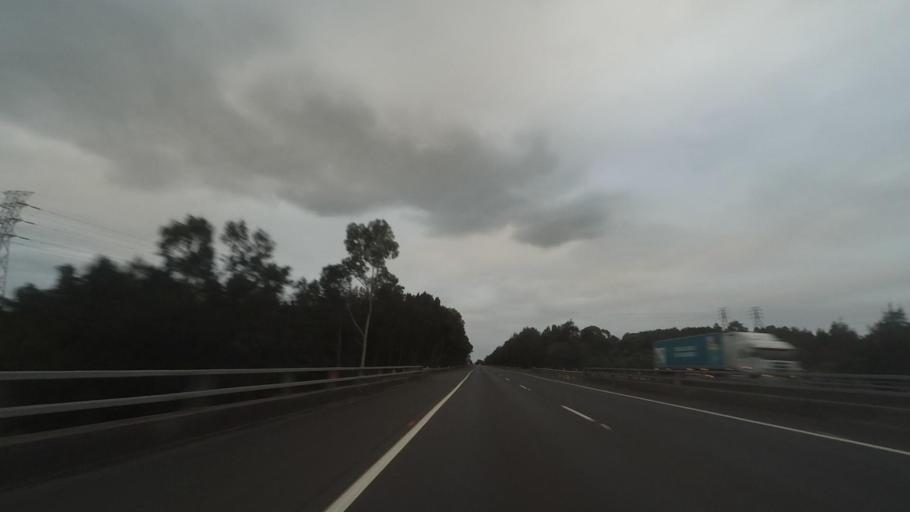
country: AU
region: New South Wales
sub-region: Wollongong
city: Berkeley
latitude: -34.4736
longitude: 150.8318
